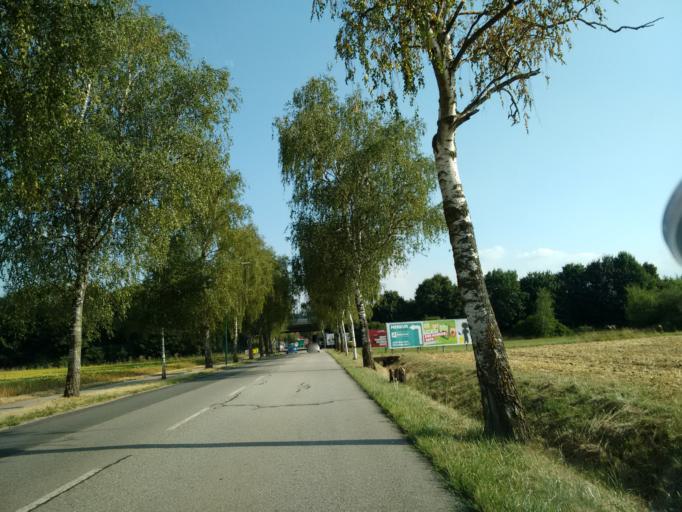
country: AT
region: Upper Austria
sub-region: Wels Stadt
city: Wels
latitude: 48.1846
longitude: 14.0146
